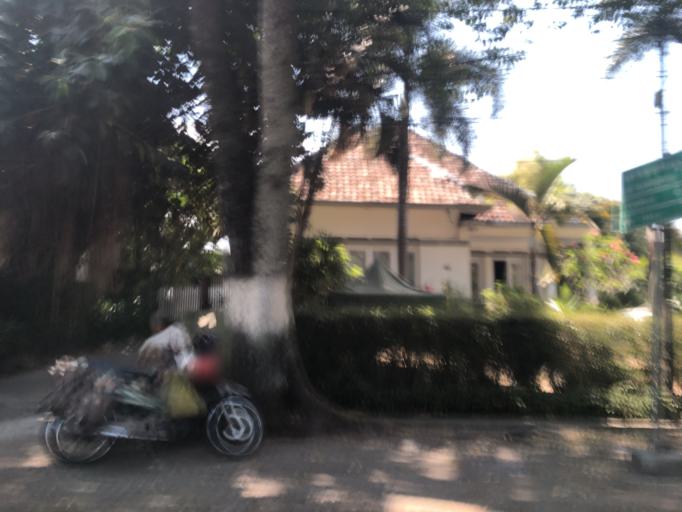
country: ID
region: West Java
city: Bandung
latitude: -6.9121
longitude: 107.6293
